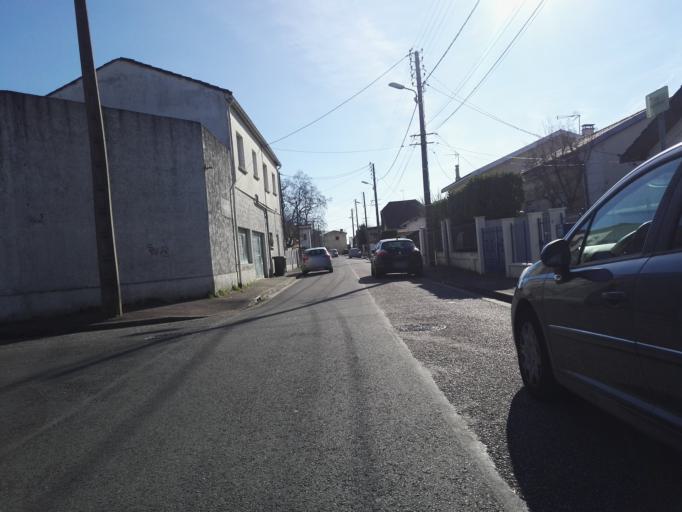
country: FR
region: Aquitaine
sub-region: Departement de la Gironde
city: Merignac
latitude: 44.8300
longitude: -0.6227
